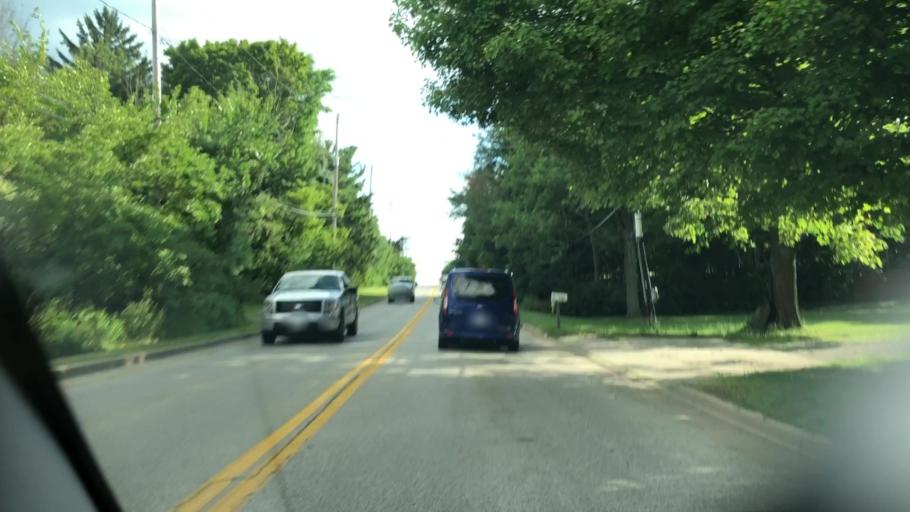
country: US
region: Ohio
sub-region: Summit County
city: Fairlawn
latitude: 41.1156
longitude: -81.6414
